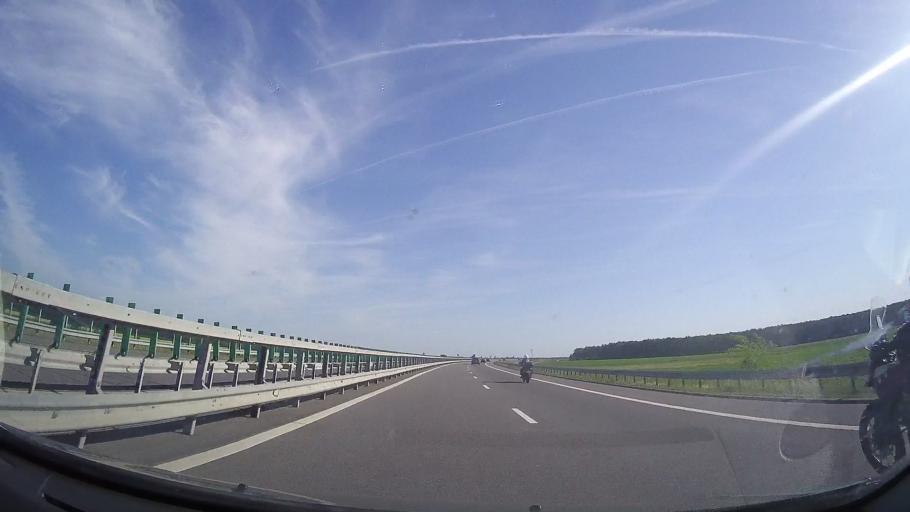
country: RO
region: Ilfov
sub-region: Comuna Gruiu
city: Gruiu
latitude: 44.6948
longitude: 26.2233
